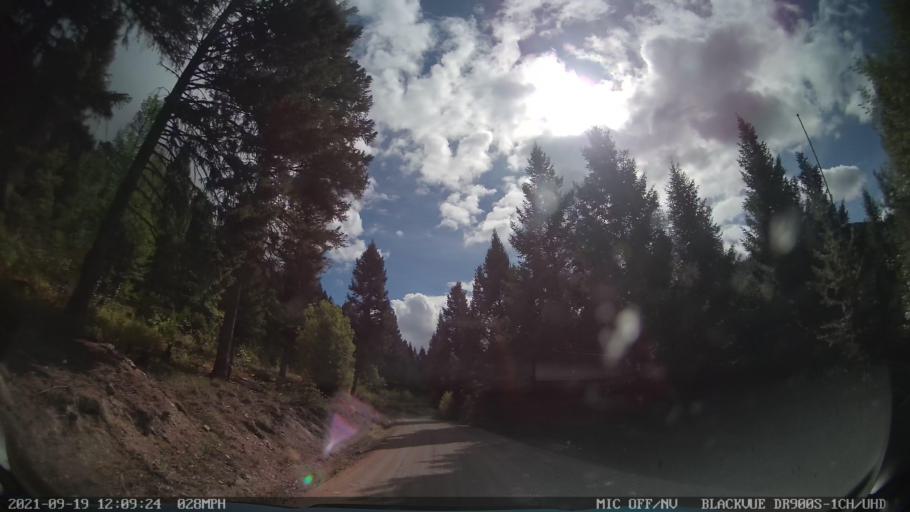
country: US
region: Montana
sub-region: Missoula County
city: Seeley Lake
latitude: 47.1836
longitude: -113.3914
